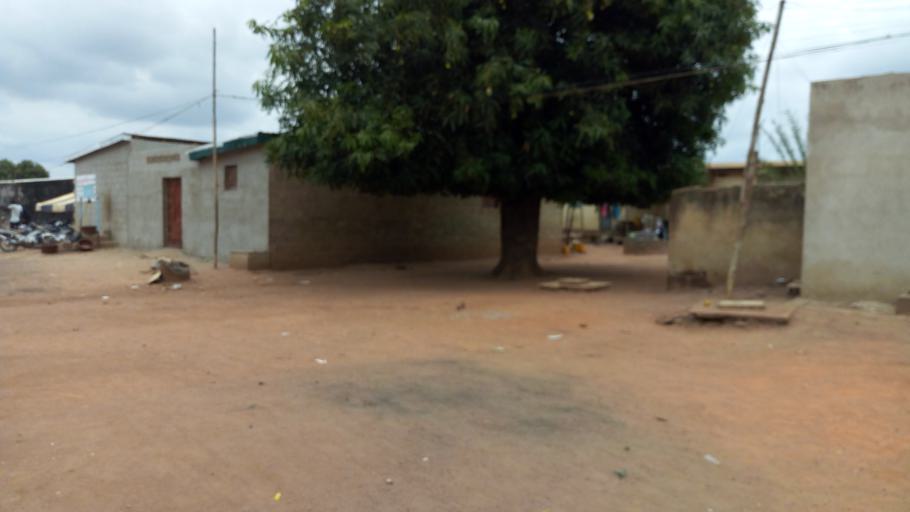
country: CI
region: Vallee du Bandama
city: Bouake
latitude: 7.7298
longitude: -5.0423
